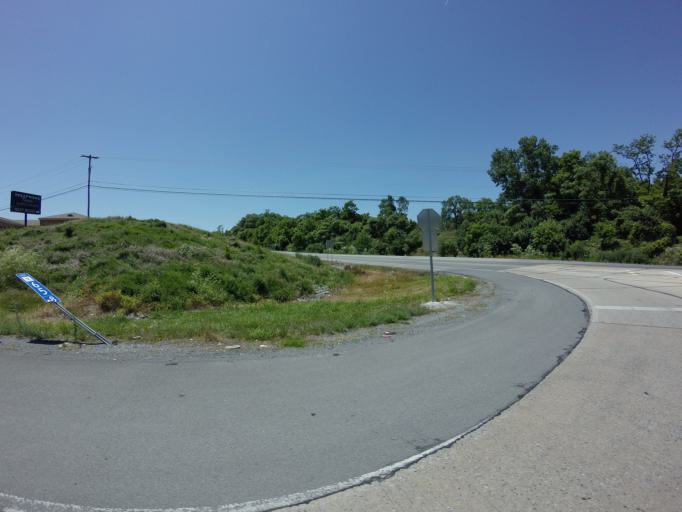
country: US
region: West Virginia
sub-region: Jefferson County
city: Ranson
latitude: 39.3053
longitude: -77.8415
